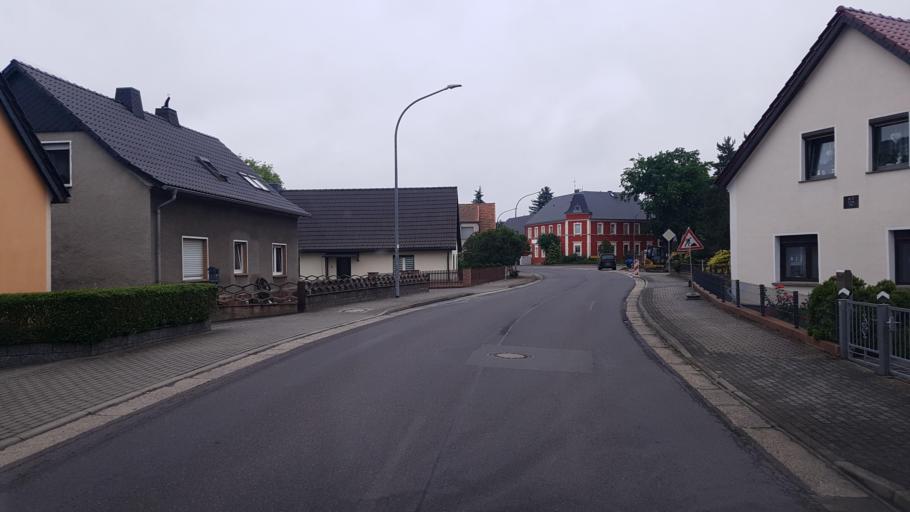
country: DE
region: Brandenburg
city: Hermsdorf
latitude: 51.4004
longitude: 13.8525
